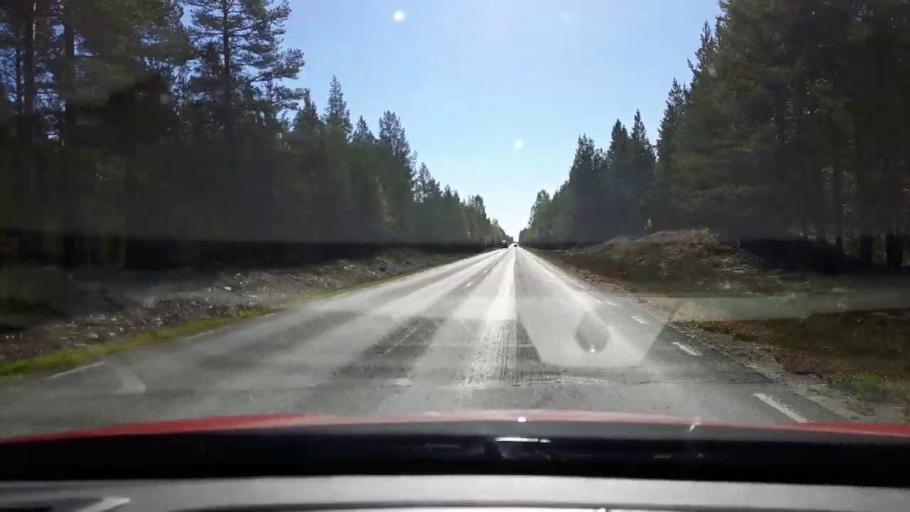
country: SE
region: Jaemtland
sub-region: Harjedalens Kommun
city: Sveg
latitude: 62.4206
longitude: 13.9079
